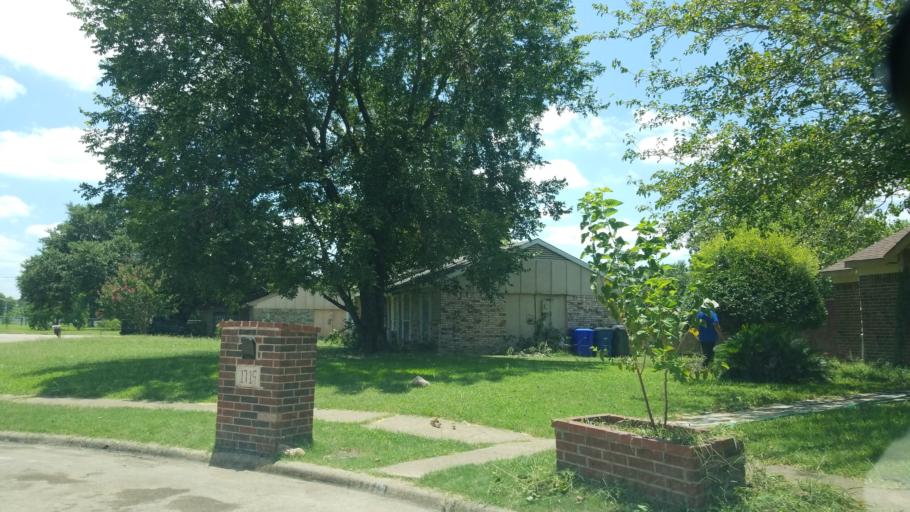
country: US
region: Texas
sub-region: Dallas County
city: Balch Springs
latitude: 32.7424
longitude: -96.7009
